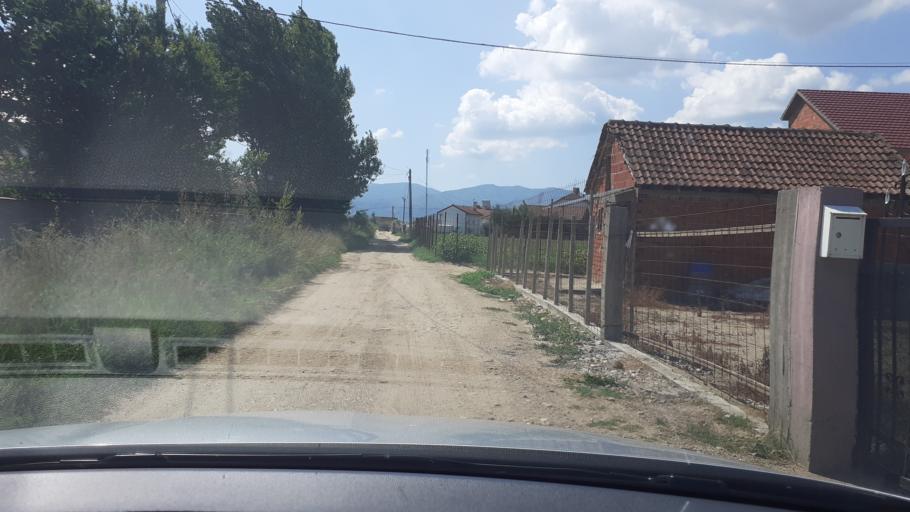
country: MK
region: Vasilevo
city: Vasilevo
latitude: 41.4694
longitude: 22.6423
